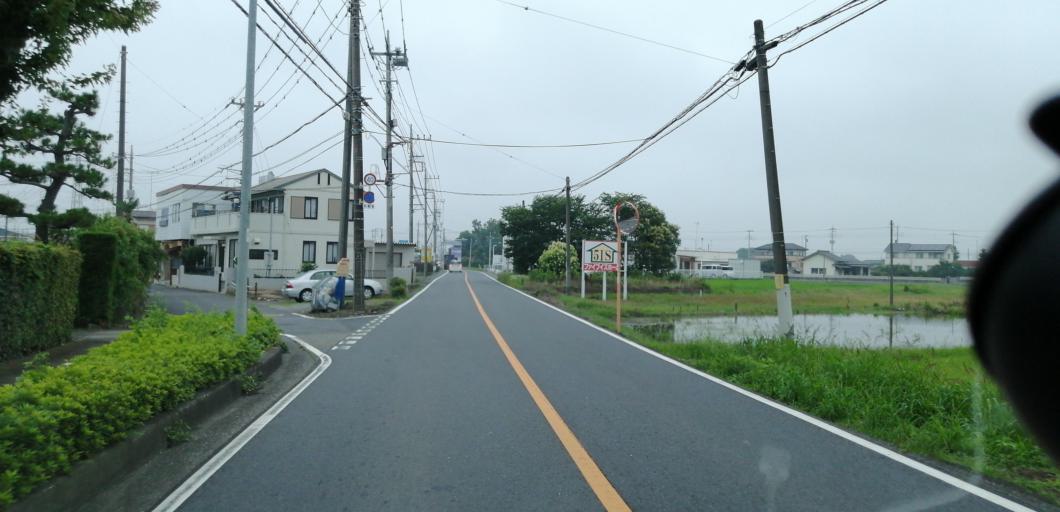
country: JP
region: Saitama
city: Kazo
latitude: 36.1220
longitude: 139.6256
